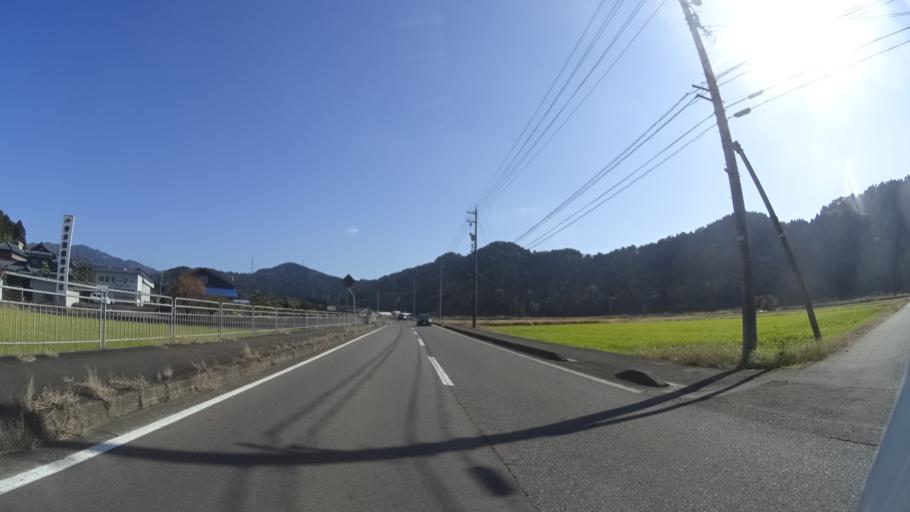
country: JP
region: Fukui
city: Sabae
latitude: 35.9470
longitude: 136.2630
